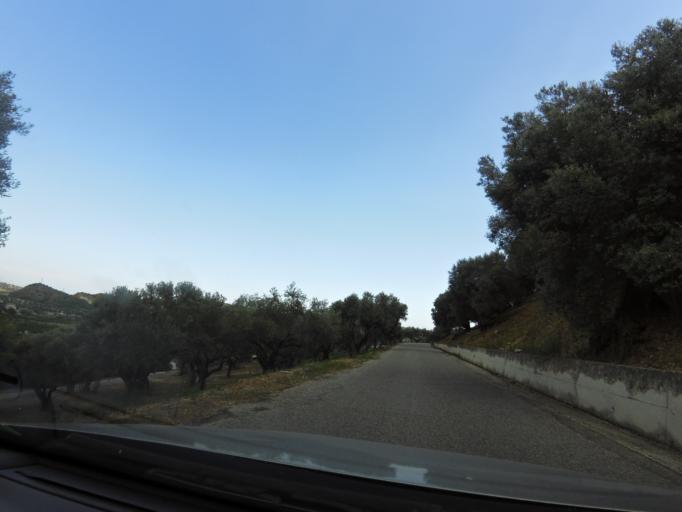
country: IT
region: Calabria
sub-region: Provincia di Reggio Calabria
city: Camini
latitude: 38.4607
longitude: 16.5029
